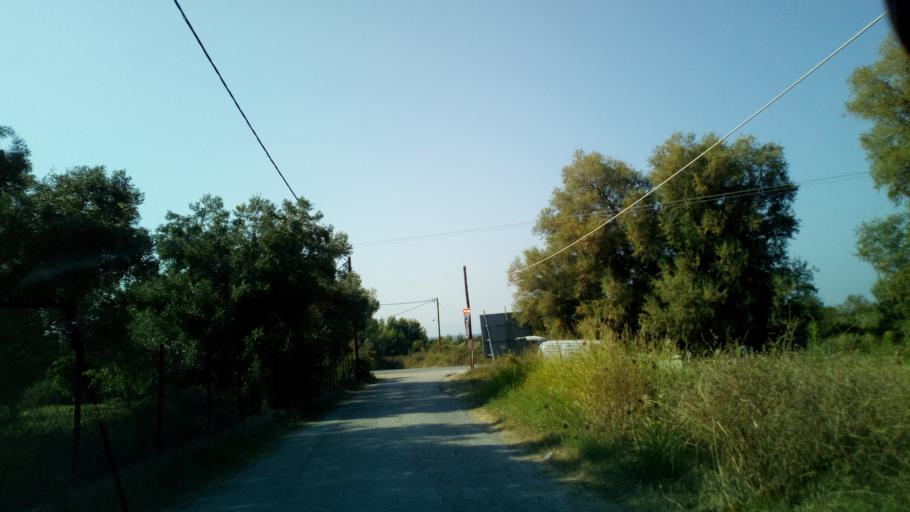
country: GR
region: Central Macedonia
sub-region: Nomos Chalkidikis
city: Pefkochori
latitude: 39.9771
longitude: 23.6513
